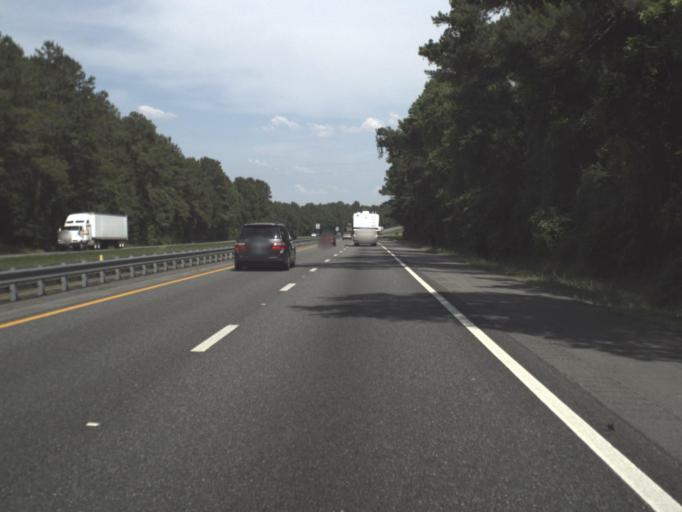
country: US
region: Florida
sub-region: Suwannee County
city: Wellborn
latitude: 30.2643
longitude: -82.7435
